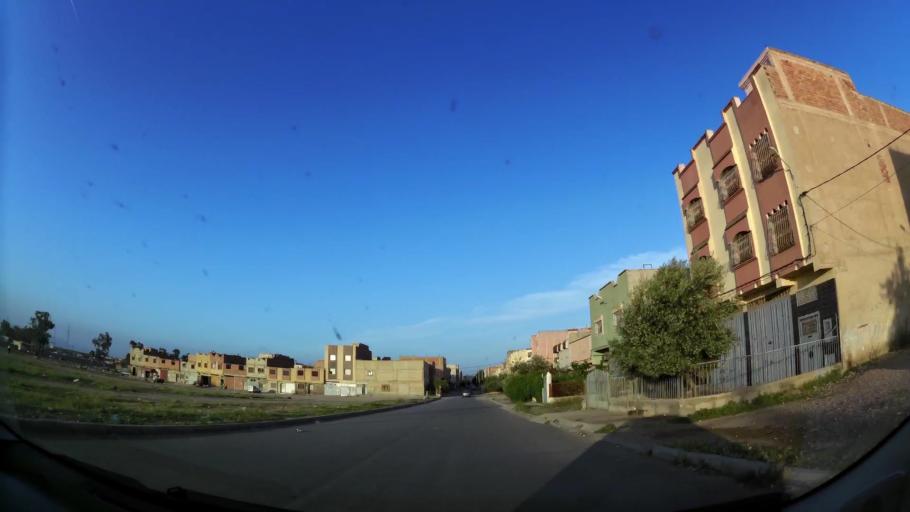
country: MA
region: Oriental
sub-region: Oujda-Angad
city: Oujda
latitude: 34.7093
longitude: -1.9145
